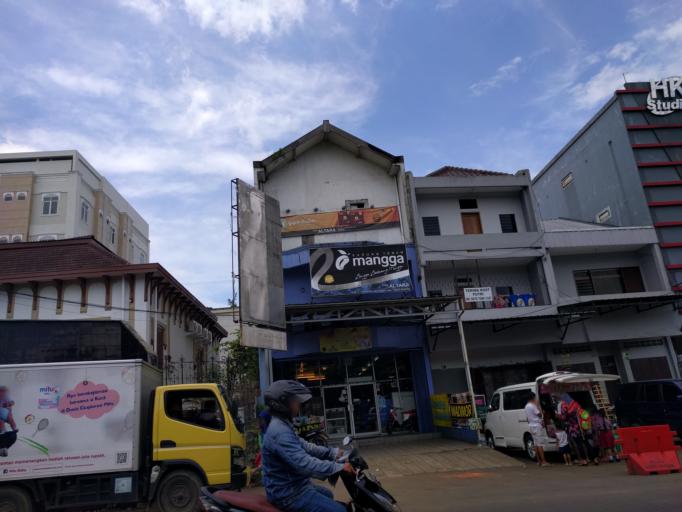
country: ID
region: West Java
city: Bogor
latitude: -6.6036
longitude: 106.7976
